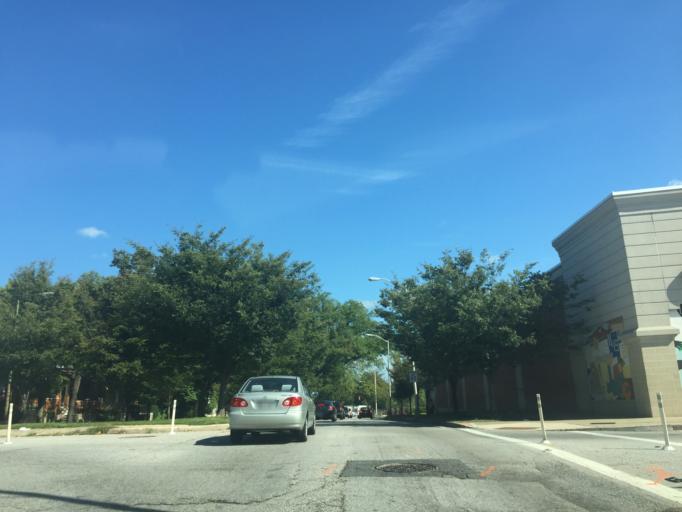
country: US
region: Maryland
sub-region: City of Baltimore
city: Baltimore
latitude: 39.3283
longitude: -76.6087
